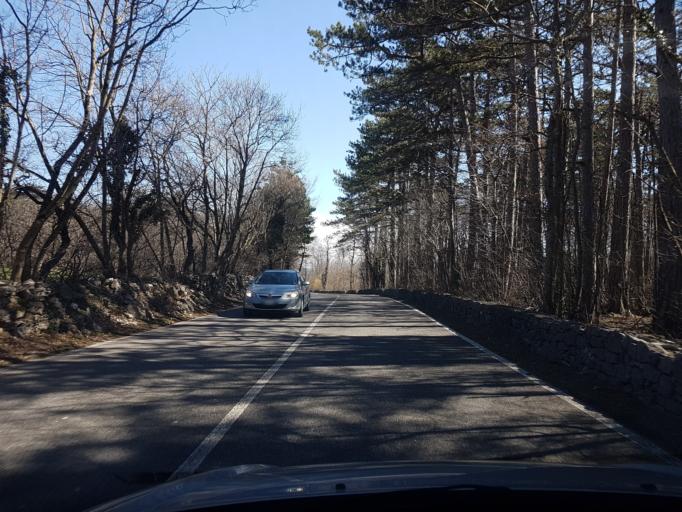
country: IT
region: Friuli Venezia Giulia
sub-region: Provincia di Trieste
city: Domio
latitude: 45.6491
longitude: 13.8505
